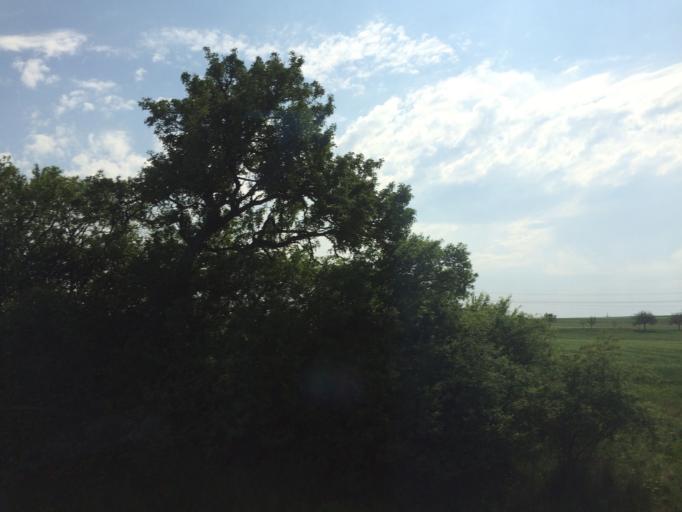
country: DE
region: Bavaria
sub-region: Regierungsbezirk Unterfranken
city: Iphofen
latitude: 49.6915
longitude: 10.2675
